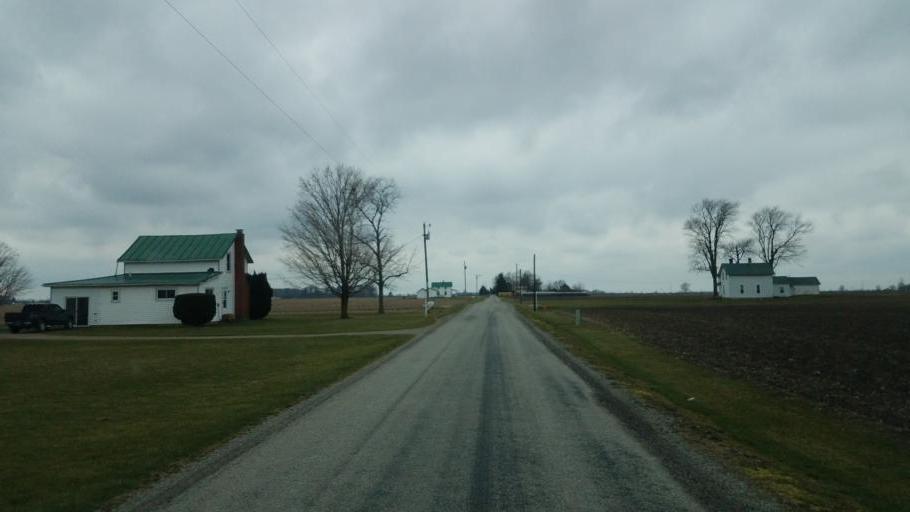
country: US
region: Ohio
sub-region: Delaware County
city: Ashley
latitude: 40.3762
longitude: -82.9675
